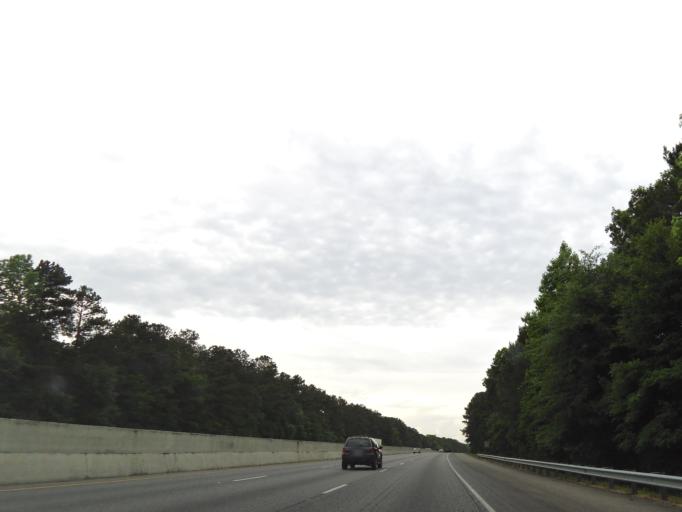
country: US
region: Georgia
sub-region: Bibb County
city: West Point
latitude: 32.9076
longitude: -83.7920
